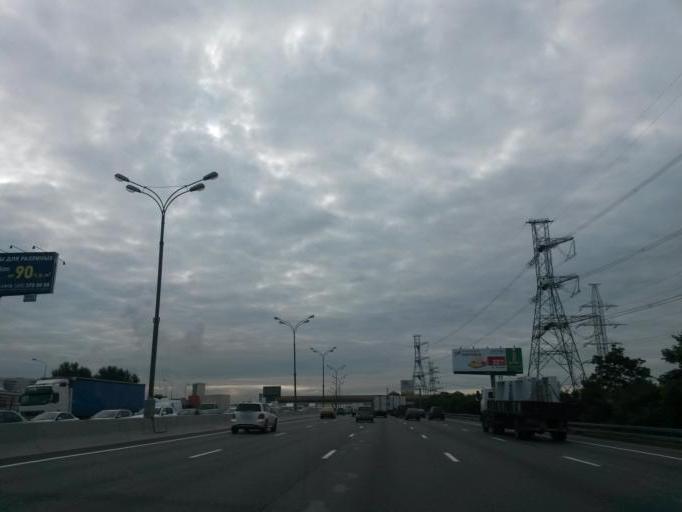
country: RU
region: Moscow
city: Annino
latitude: 55.5776
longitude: 37.5865
